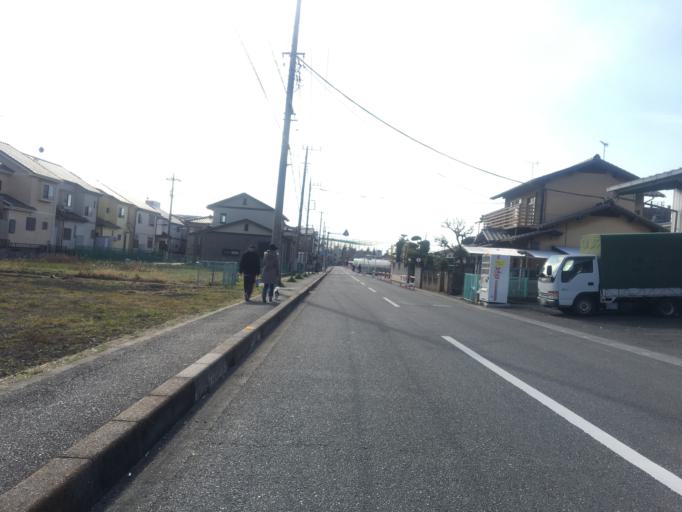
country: JP
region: Saitama
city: Shiki
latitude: 35.8408
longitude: 139.5870
